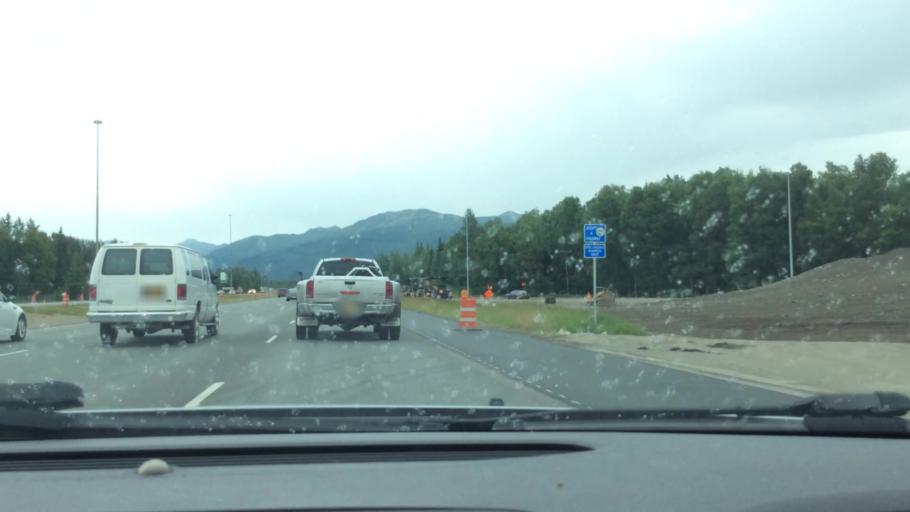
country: US
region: Alaska
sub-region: Anchorage Municipality
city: Elmendorf Air Force Base
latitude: 61.2275
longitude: -149.7319
